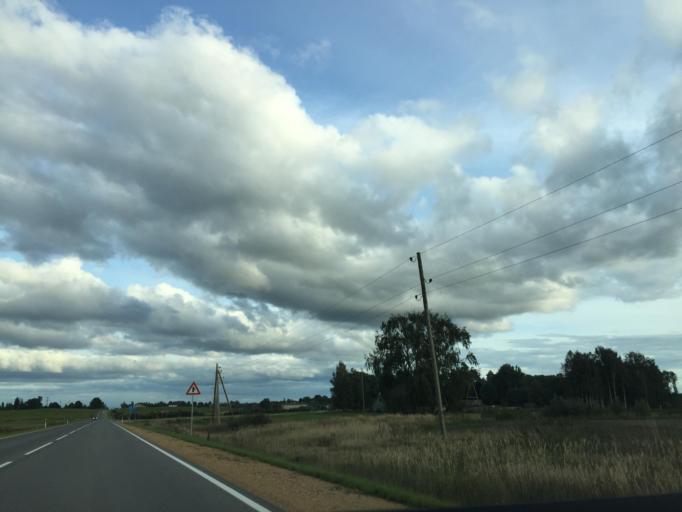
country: LV
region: Nereta
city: Nereta
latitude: 56.2181
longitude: 25.2935
